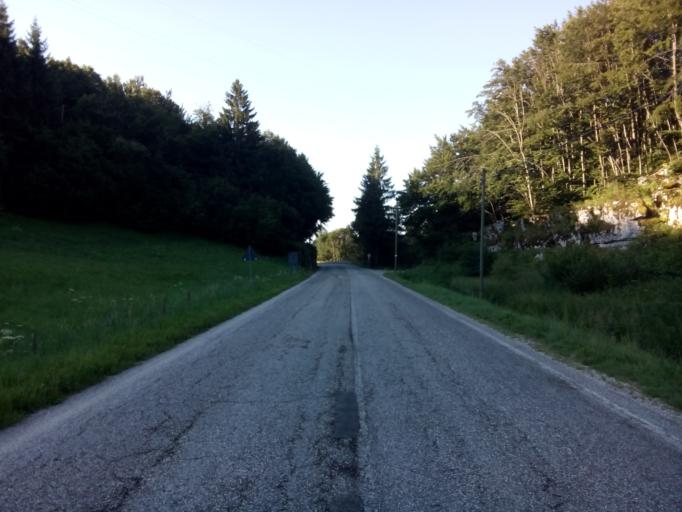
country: IT
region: Veneto
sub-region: Provincia di Vicenza
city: Conco
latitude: 45.8170
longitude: 11.6095
